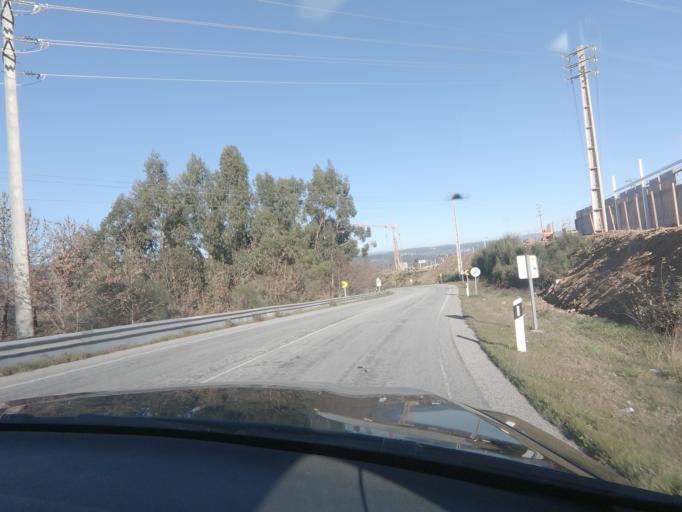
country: PT
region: Viseu
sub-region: Vouzela
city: Vouzela
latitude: 40.7233
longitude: -8.1328
